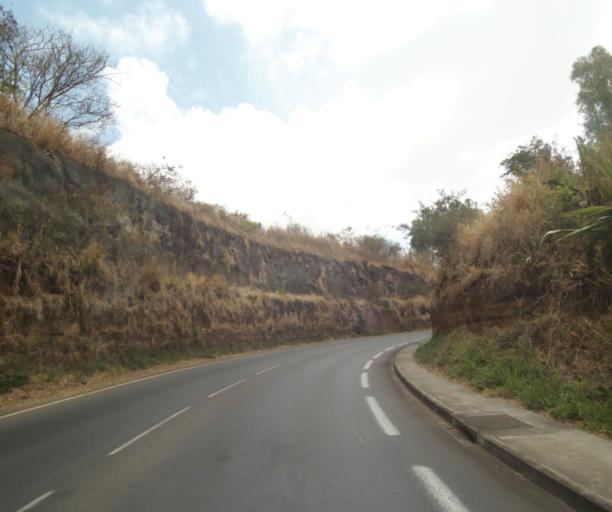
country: RE
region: Reunion
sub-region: Reunion
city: Saint-Paul
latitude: -21.0540
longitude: 55.2681
